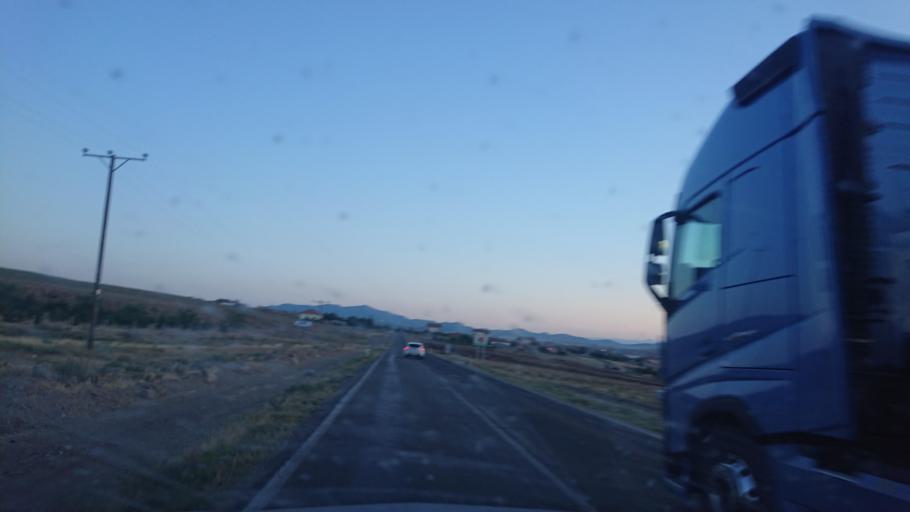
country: TR
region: Aksaray
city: Balci
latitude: 38.7992
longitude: 34.1286
